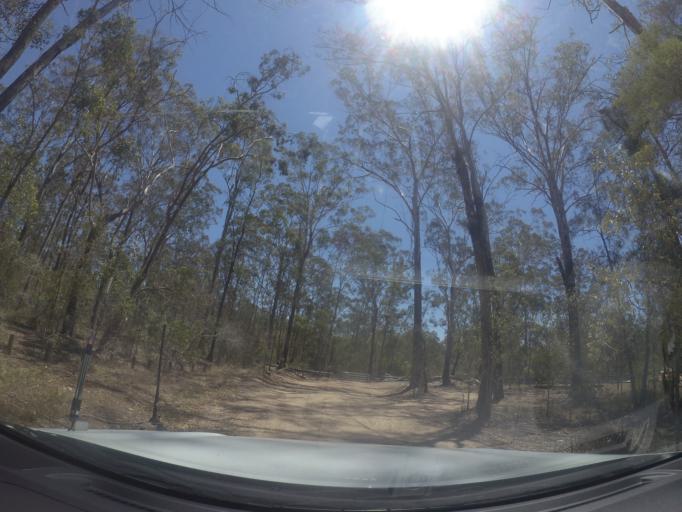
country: AU
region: Queensland
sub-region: Logan
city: Chambers Flat
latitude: -27.7781
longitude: 153.1251
